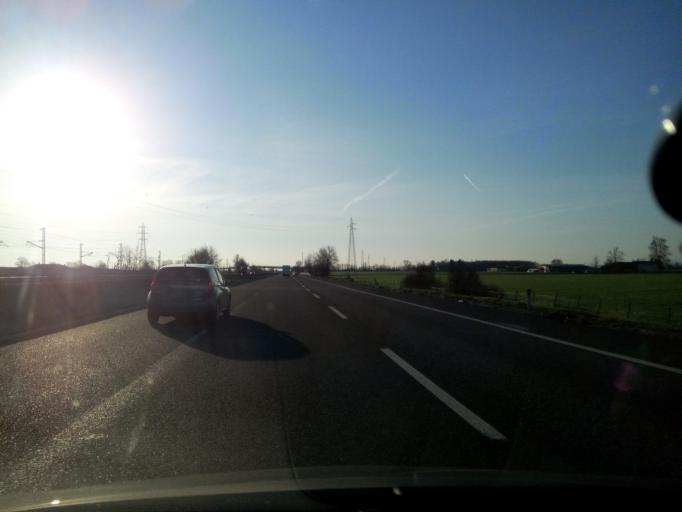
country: IT
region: Emilia-Romagna
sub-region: Provincia di Piacenza
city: Pontenure
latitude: 45.0020
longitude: 9.8095
